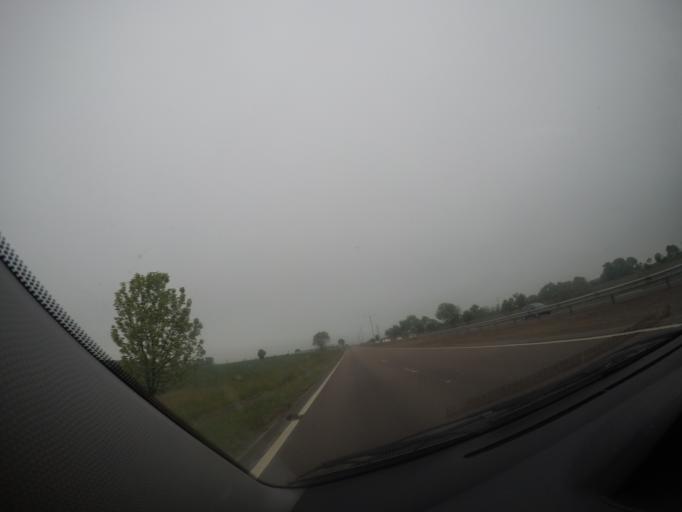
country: GB
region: Scotland
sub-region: Dundee City
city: Dundee
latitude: 56.5155
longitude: -2.9454
